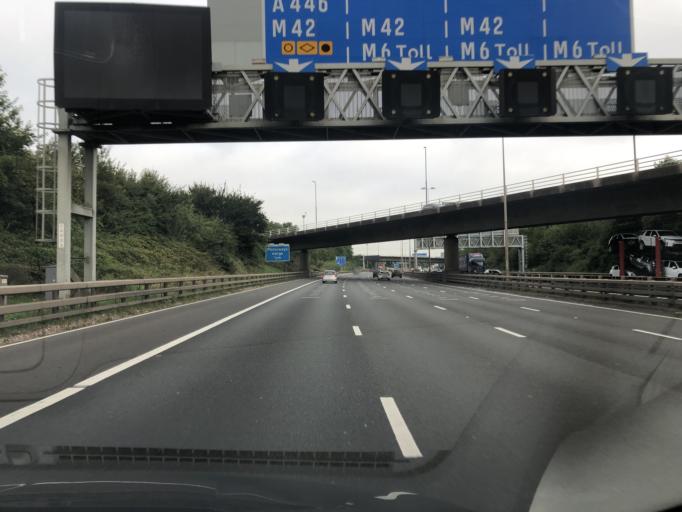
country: GB
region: England
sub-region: Warwickshire
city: Water Orton
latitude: 52.5068
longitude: -1.7247
